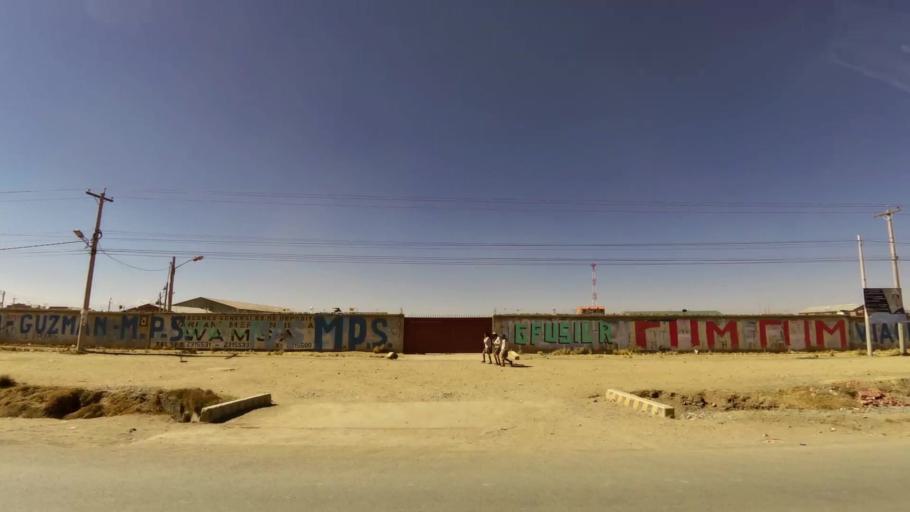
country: BO
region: La Paz
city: La Paz
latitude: -16.5780
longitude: -68.2308
